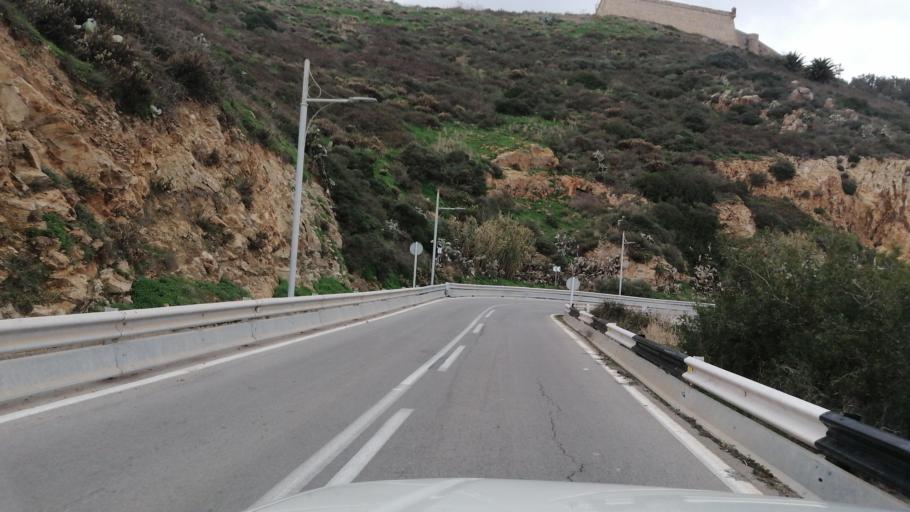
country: ES
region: Ceuta
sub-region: Ceuta
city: Ceuta
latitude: 35.8915
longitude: -5.2916
